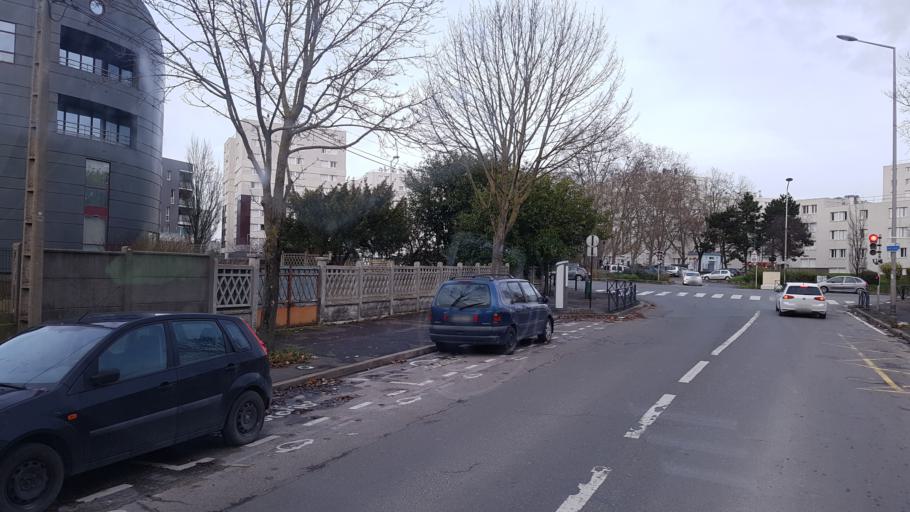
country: FR
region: Ile-de-France
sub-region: Departement de Seine-Saint-Denis
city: Aulnay-sous-Bois
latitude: 48.9489
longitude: 2.4884
